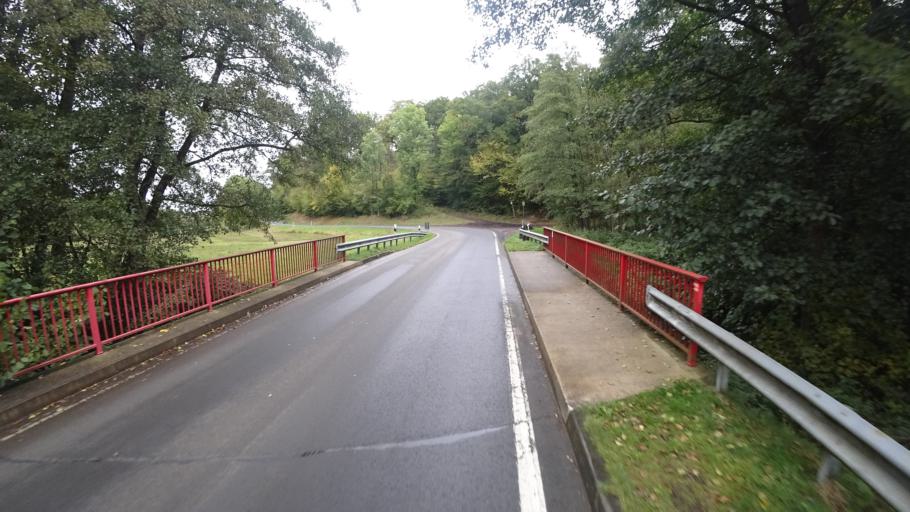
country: DE
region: Rheinland-Pfalz
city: Oberhaid
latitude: 50.5088
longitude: 7.7217
